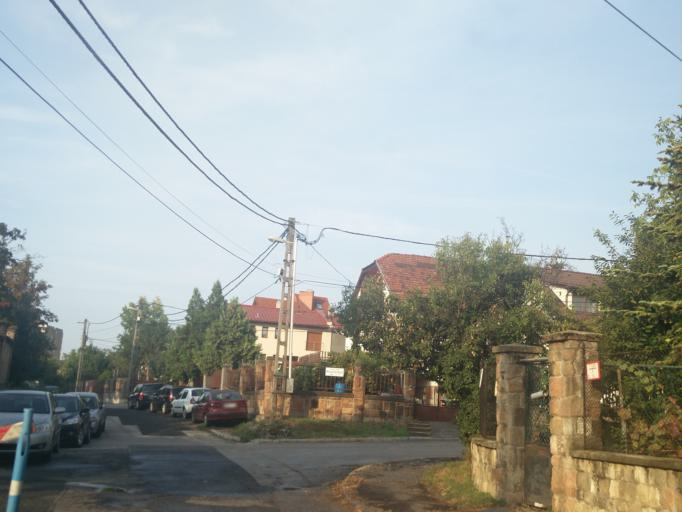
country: HU
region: Budapest
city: Budapest XI. keruelet
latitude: 47.4786
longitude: 19.0217
